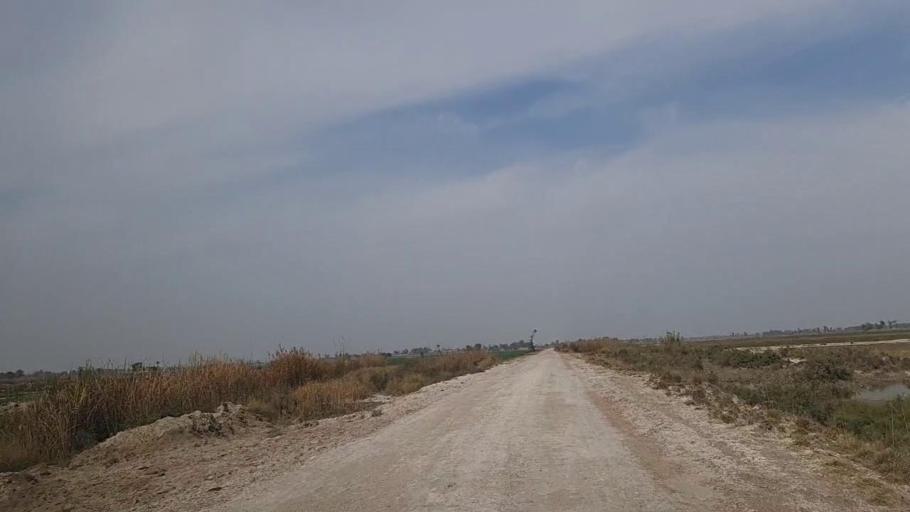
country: PK
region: Sindh
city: Daur
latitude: 26.4705
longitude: 68.4024
